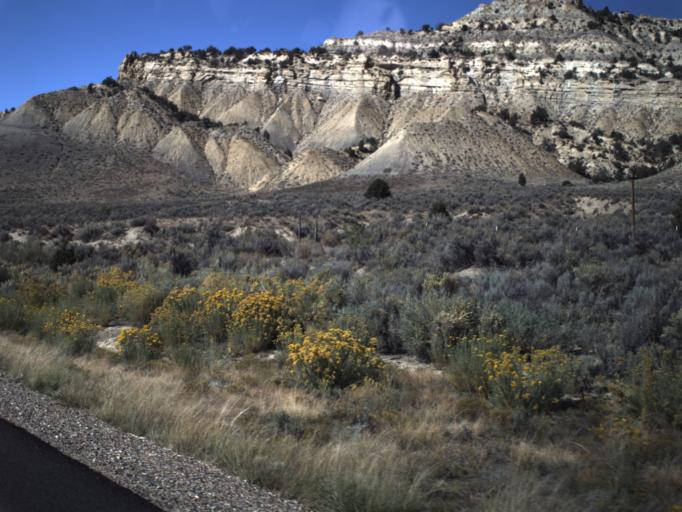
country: US
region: Utah
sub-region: Garfield County
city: Panguitch
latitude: 37.5924
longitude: -111.9323
